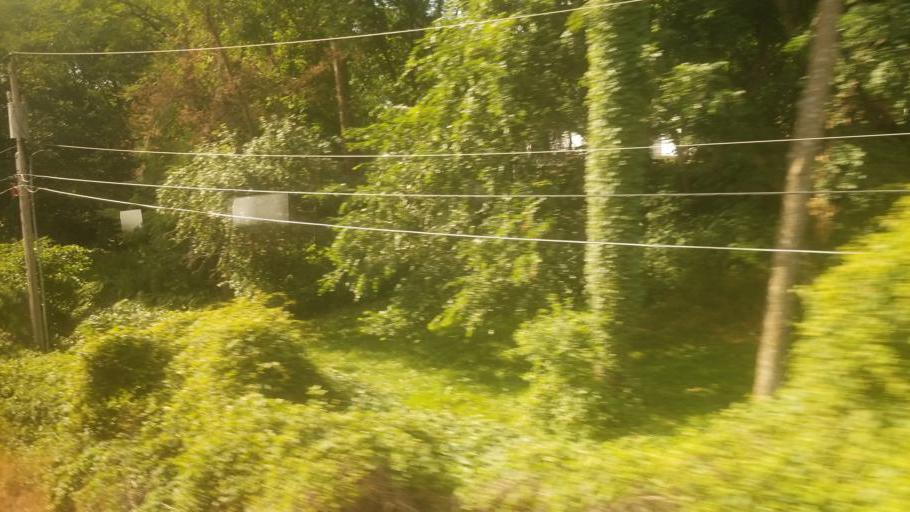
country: US
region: Kansas
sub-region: Wyandotte County
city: Edwardsville
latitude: 39.0472
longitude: -94.8276
